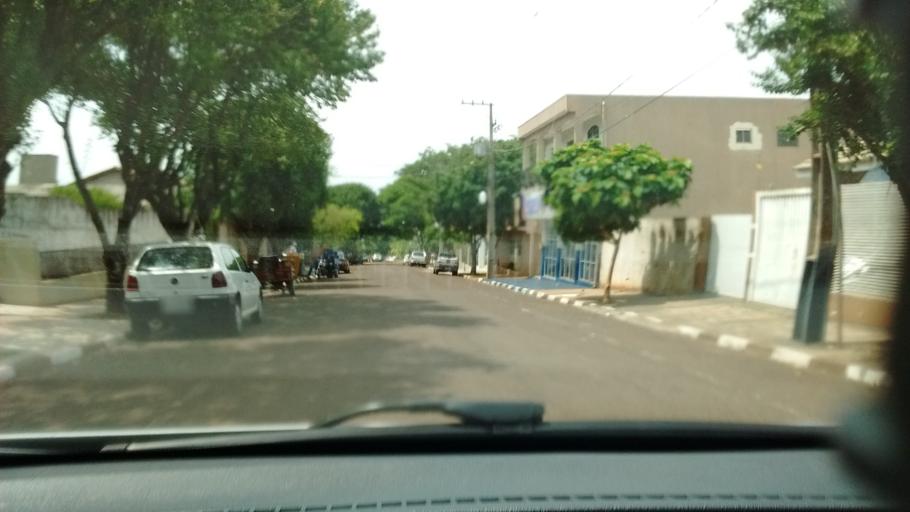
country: BR
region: Parana
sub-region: Corbelia
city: Corbelia
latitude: -24.5413
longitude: -52.9912
